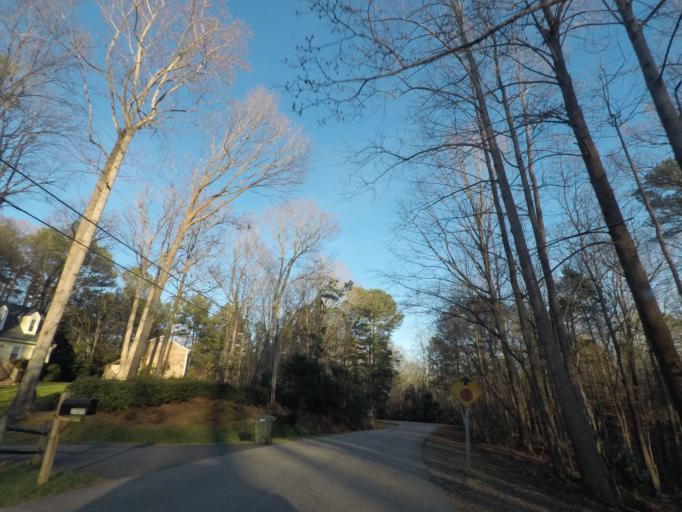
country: US
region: North Carolina
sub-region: Durham County
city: Durham
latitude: 36.0840
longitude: -78.9722
